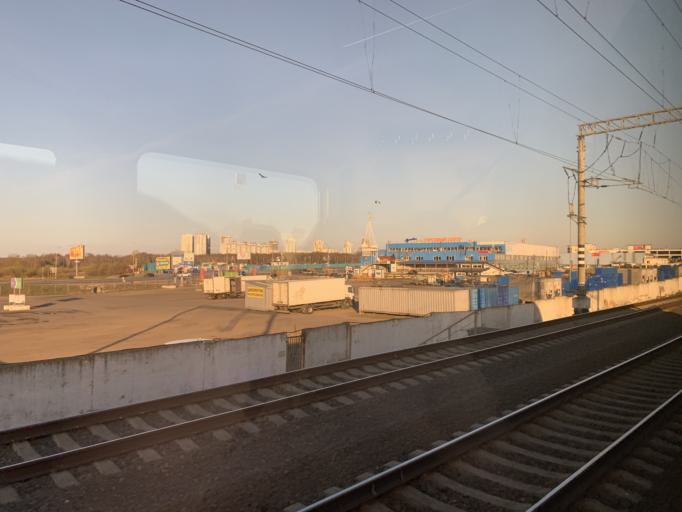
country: BY
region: Minsk
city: Zhdanovichy
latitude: 53.9410
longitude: 27.4373
